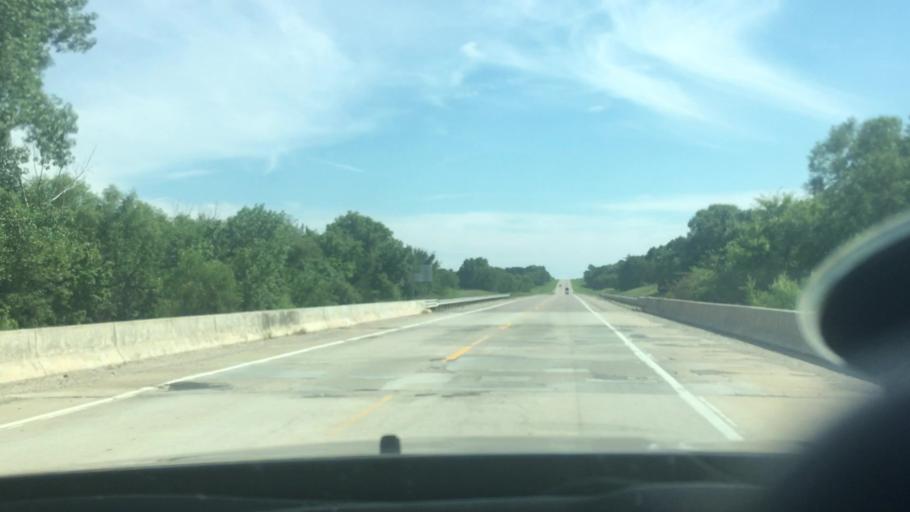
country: US
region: Oklahoma
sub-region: Seminole County
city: Maud
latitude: 35.1278
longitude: -96.6790
